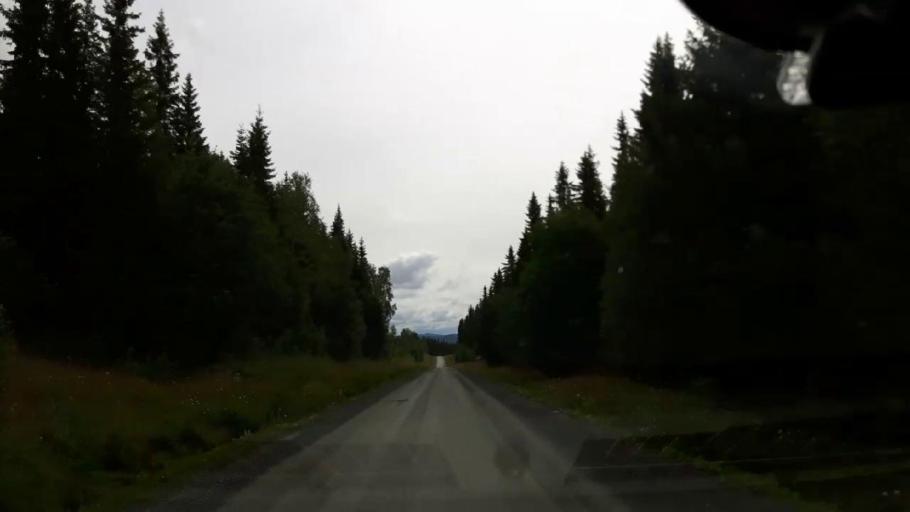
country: SE
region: Jaemtland
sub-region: Krokoms Kommun
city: Valla
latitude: 63.6497
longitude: 13.9862
